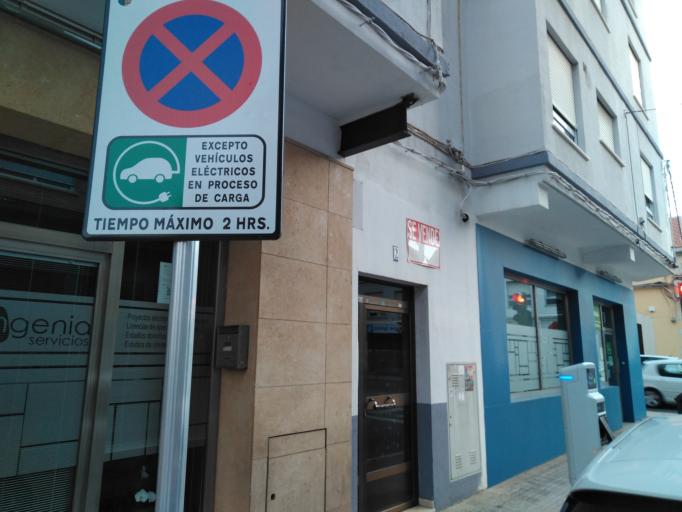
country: ES
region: Valencia
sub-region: Provincia de Valencia
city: Oliva
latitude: 38.9172
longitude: -0.1167
